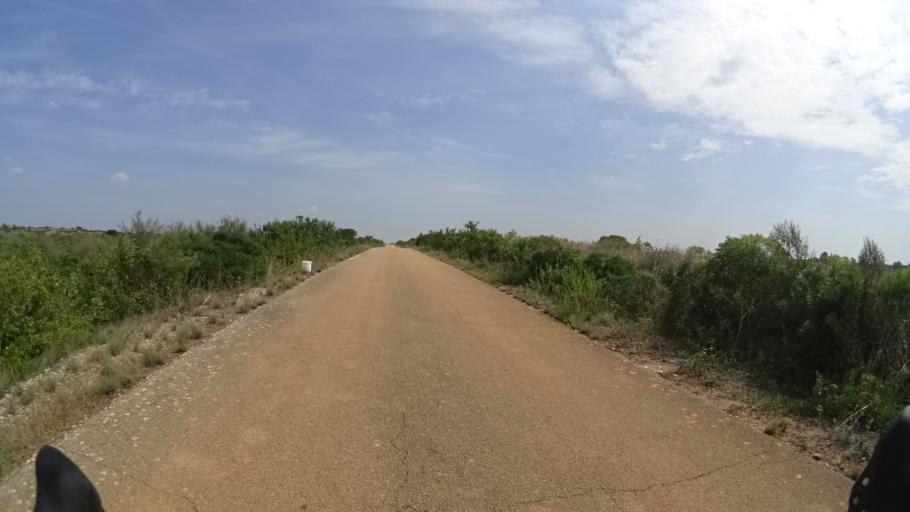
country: IT
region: Apulia
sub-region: Provincia di Brindisi
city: San Pancrazio Salentino
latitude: 40.3474
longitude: 17.8134
